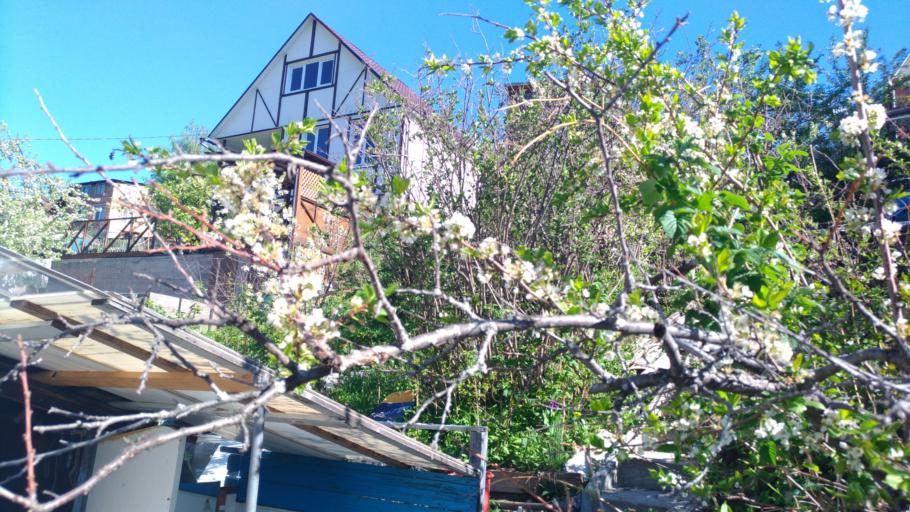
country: RU
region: Krasnoyarskiy
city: Krasnoyarsk
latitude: 56.0081
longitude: 92.7466
